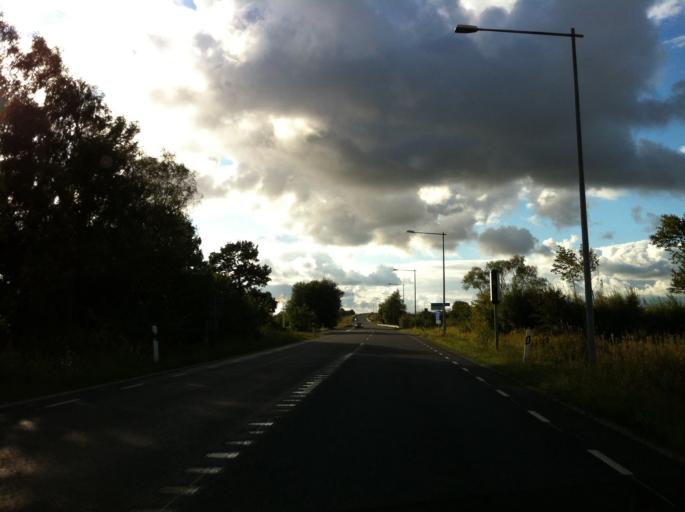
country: SE
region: Skane
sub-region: Svalovs Kommun
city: Teckomatorp
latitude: 55.8738
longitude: 13.0944
